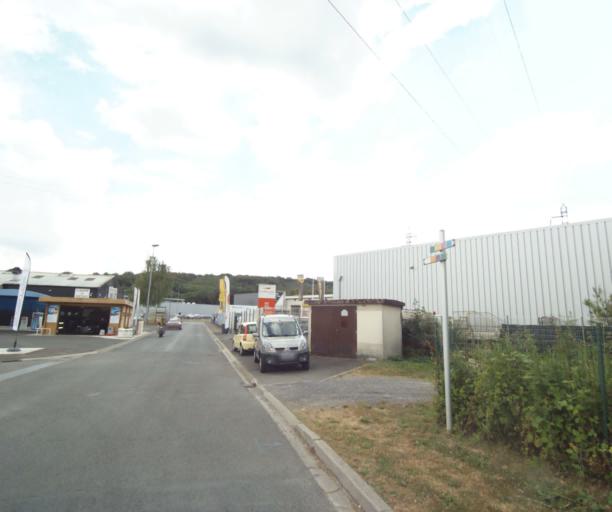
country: FR
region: Ile-de-France
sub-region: Departement de Seine-et-Marne
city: Vulaines-sur-Seine
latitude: 48.4247
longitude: 2.7687
